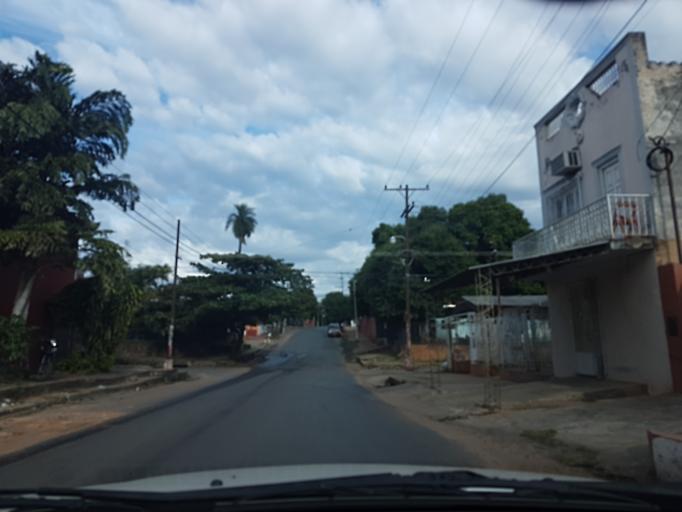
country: PY
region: Central
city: Lambare
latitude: -25.3283
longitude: -57.5813
